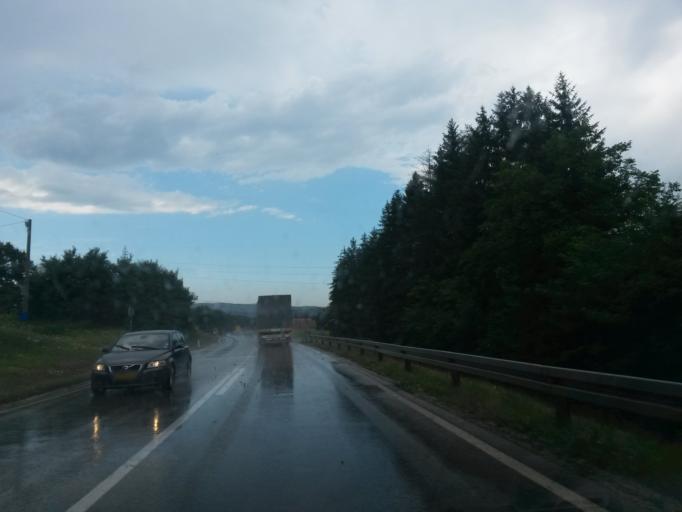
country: BA
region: Federation of Bosnia and Herzegovina
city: Lijesnica
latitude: 44.4741
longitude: 18.0692
